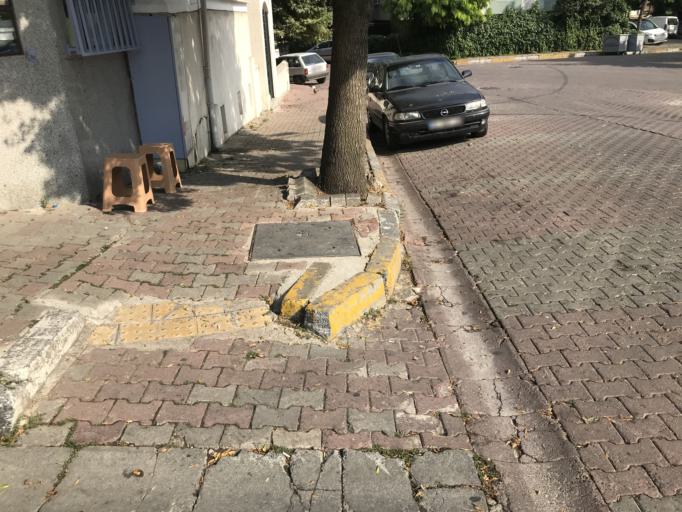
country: TR
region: Istanbul
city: Bahcelievler
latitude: 40.9988
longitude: 28.8619
